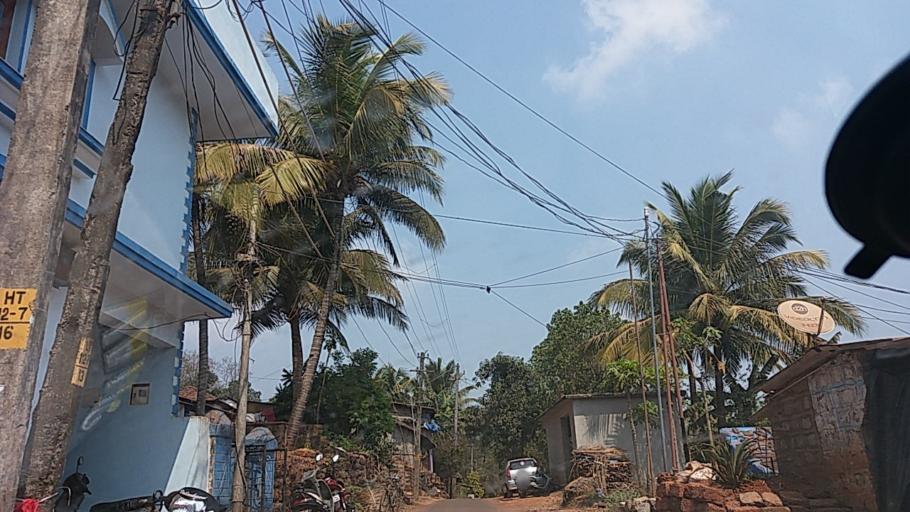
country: IN
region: Goa
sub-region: South Goa
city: Sancoale
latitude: 15.3711
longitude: 73.9148
